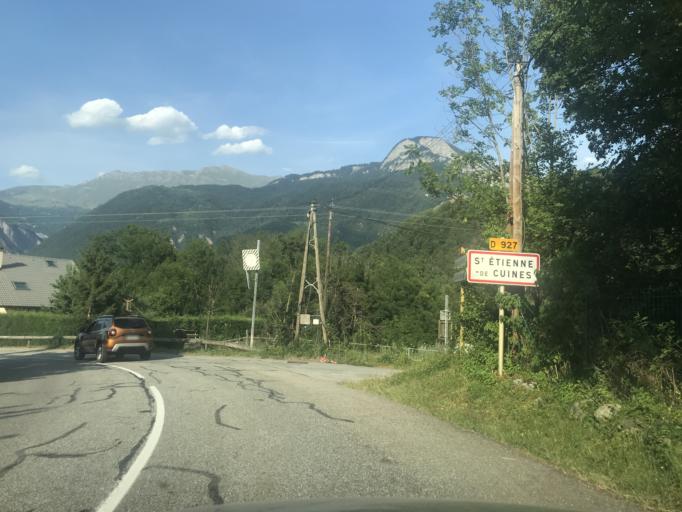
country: FR
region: Rhone-Alpes
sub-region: Departement de la Savoie
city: Saint-Etienne-de-Cuines
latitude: 45.3335
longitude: 6.2877
